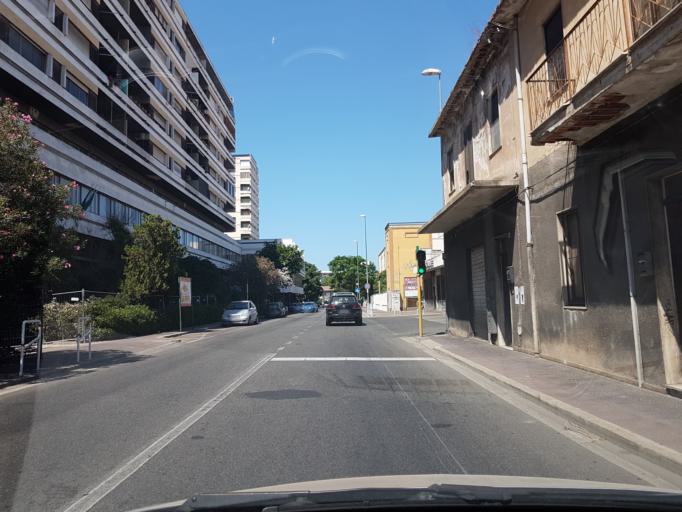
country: IT
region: Sardinia
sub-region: Provincia di Oristano
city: Oristano
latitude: 39.9011
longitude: 8.5910
